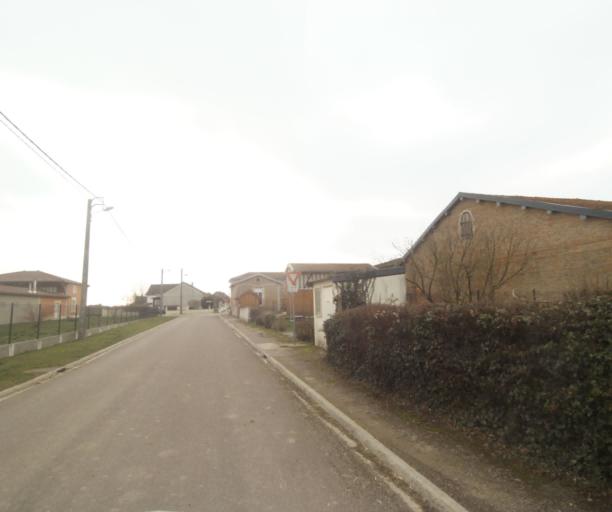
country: FR
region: Champagne-Ardenne
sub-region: Departement de la Haute-Marne
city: Villiers-en-Lieu
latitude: 48.6810
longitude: 4.8327
